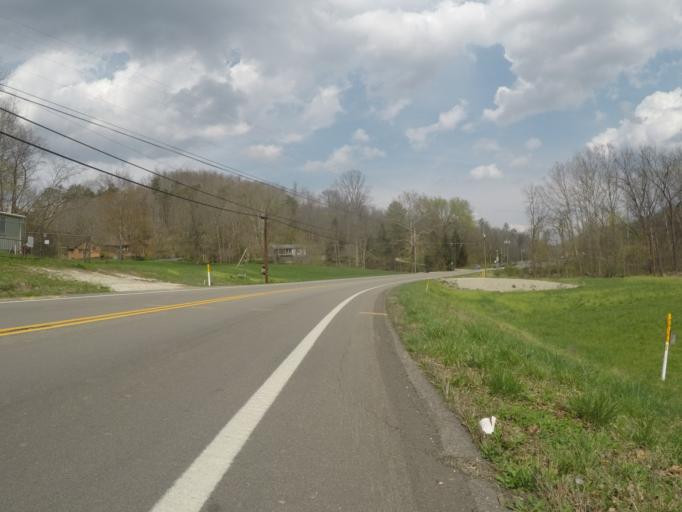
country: US
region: West Virginia
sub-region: Cabell County
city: Pea Ridge
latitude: 38.3840
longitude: -82.3341
